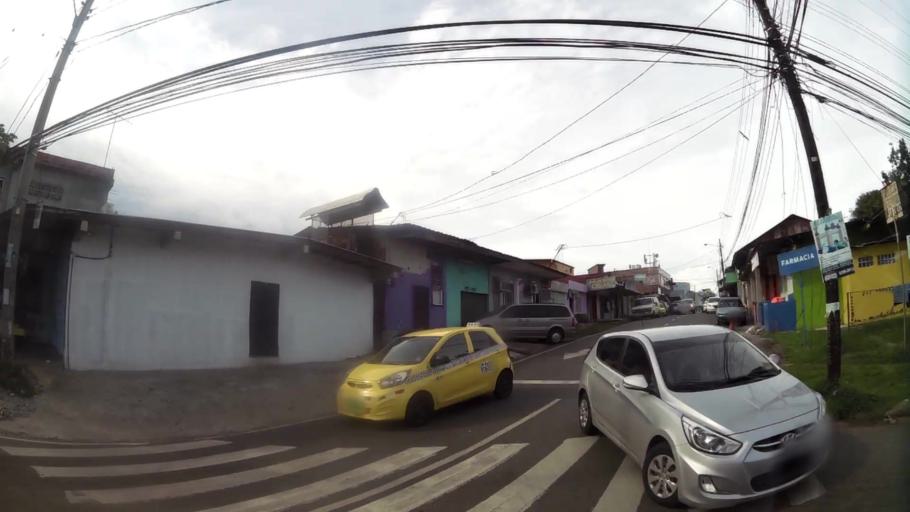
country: PA
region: Panama
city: La Chorrera
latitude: 8.8802
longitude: -79.7796
